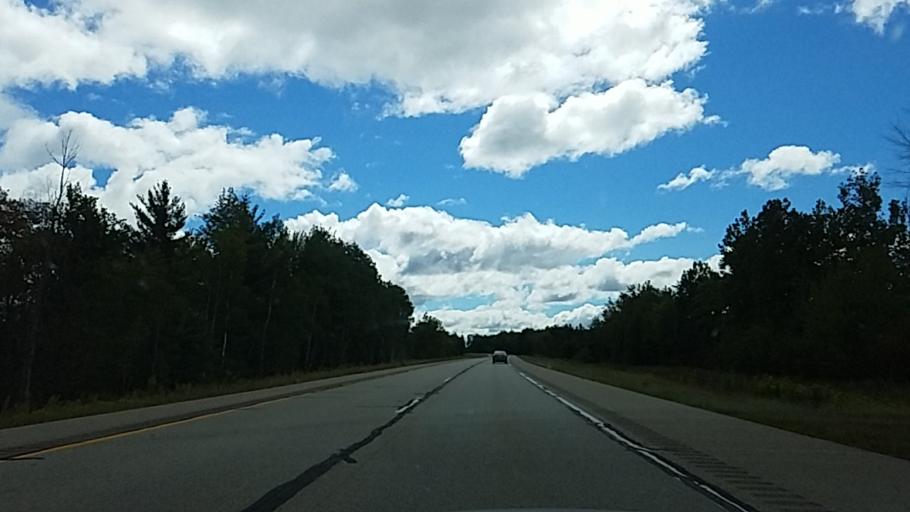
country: US
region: Michigan
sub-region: Ogemaw County
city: Skidway Lake
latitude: 44.1593
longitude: -84.1584
